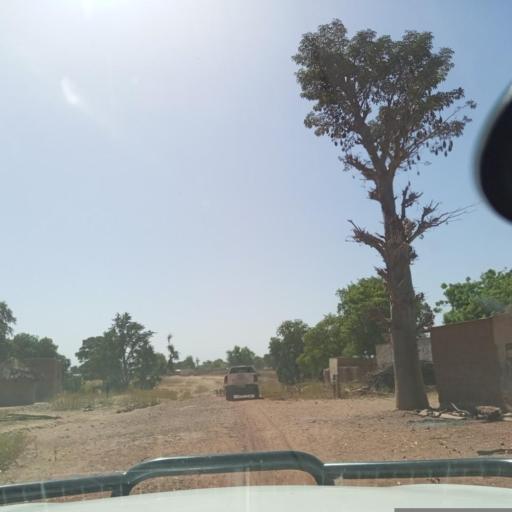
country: ML
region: Koulikoro
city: Dioila
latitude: 12.6236
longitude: -7.0245
